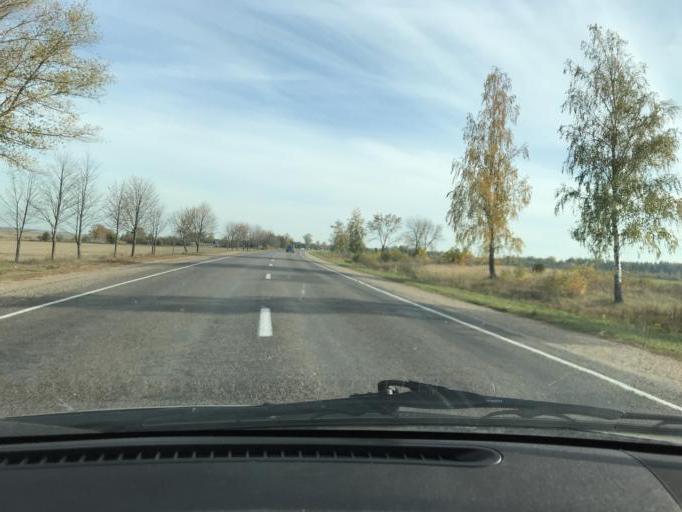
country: BY
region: Brest
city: Lahishyn
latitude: 52.2399
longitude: 26.0026
